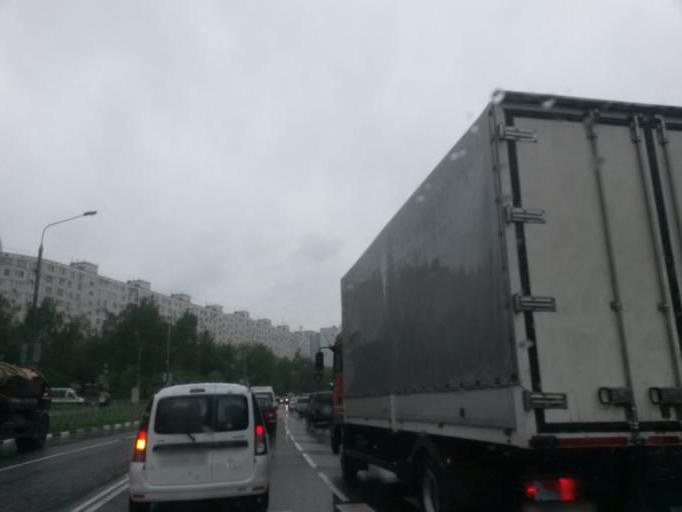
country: RU
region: Moscow
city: Zyablikovo
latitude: 55.6229
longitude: 37.7509
